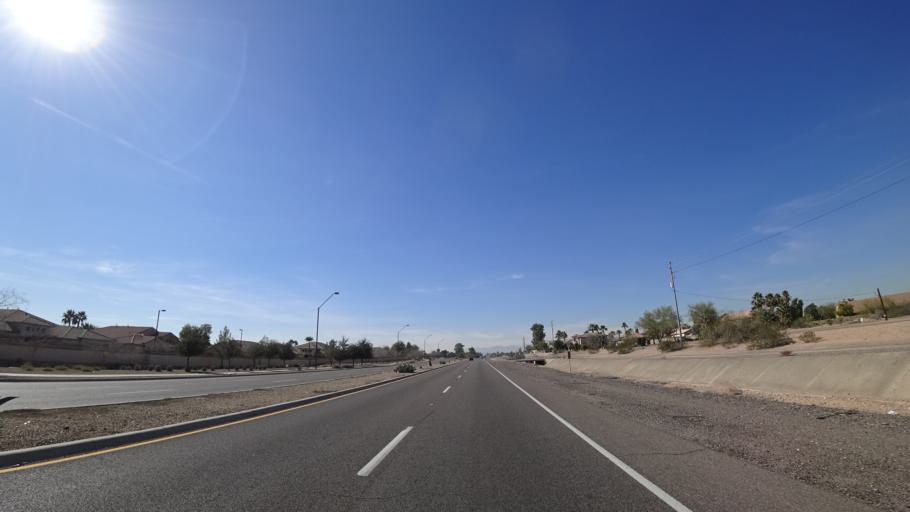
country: US
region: Arizona
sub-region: Maricopa County
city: Litchfield Park
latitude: 33.5076
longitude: -112.3345
